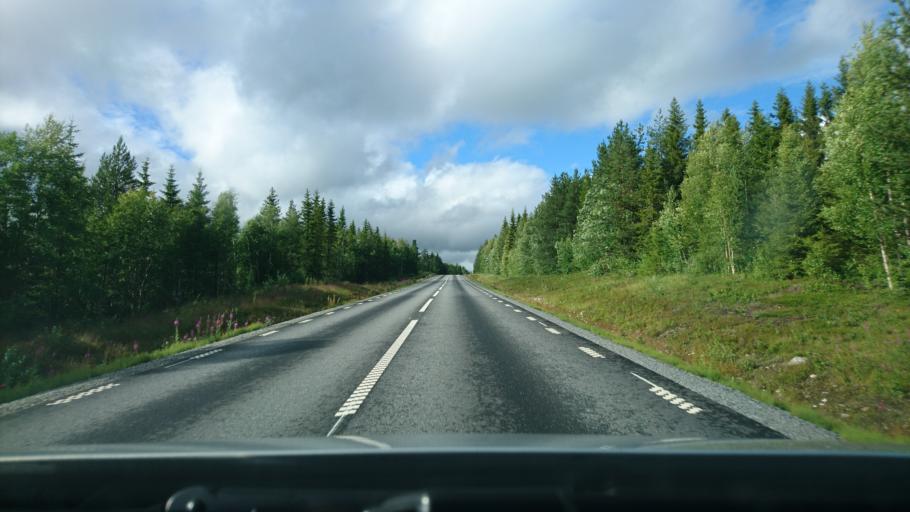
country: SE
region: Vaesterbotten
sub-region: Vilhelmina Kommun
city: Vilhelmina
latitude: 64.7103
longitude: 16.7069
